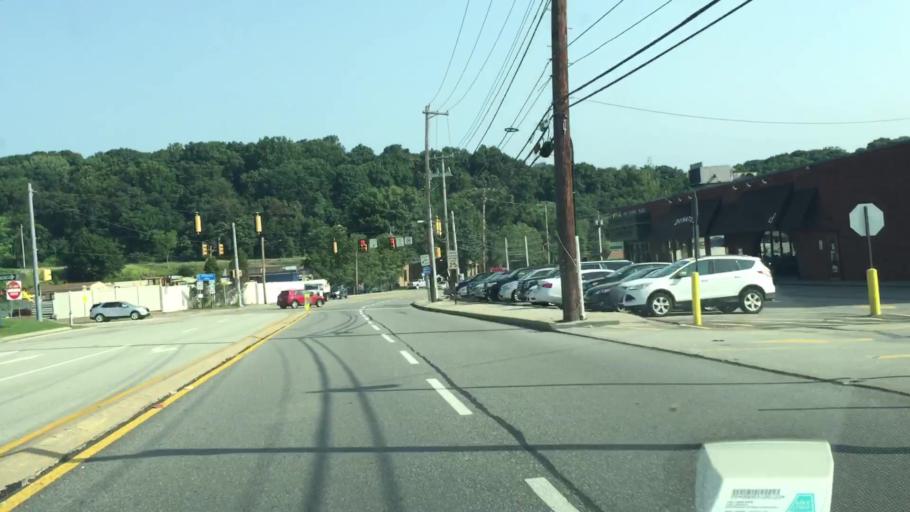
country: US
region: Pennsylvania
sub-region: Allegheny County
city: Aspinwall
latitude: 40.4878
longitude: -79.8829
